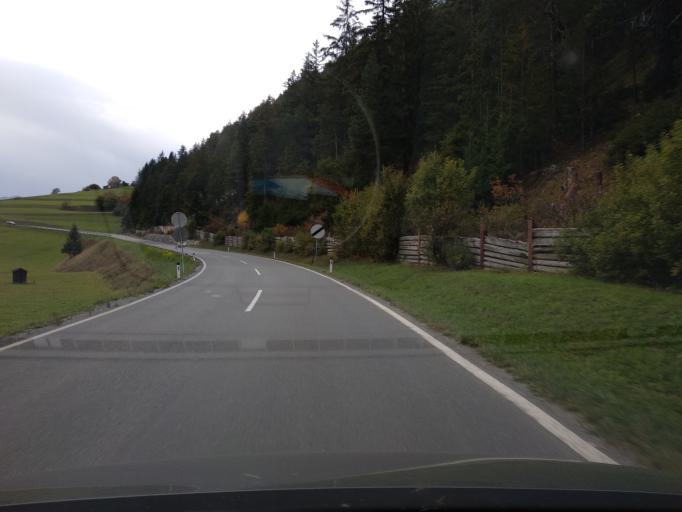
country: AT
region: Tyrol
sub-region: Politischer Bezirk Landeck
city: Flirsch
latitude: 47.1523
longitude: 10.3584
